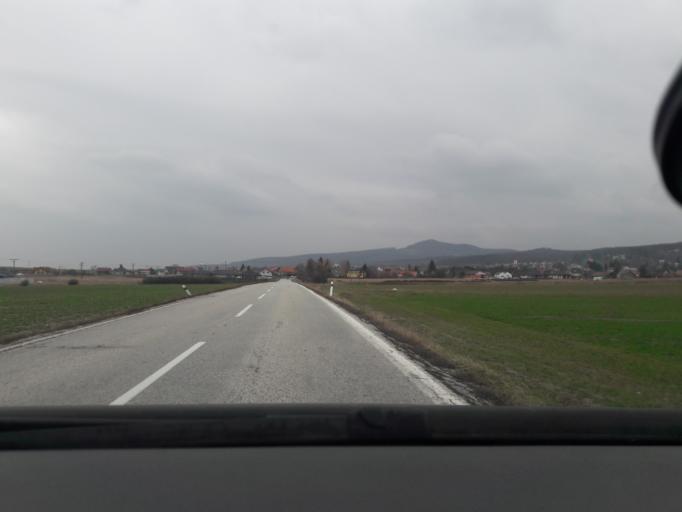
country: SK
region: Bratislavsky
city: Modra
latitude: 48.4034
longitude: 17.3727
